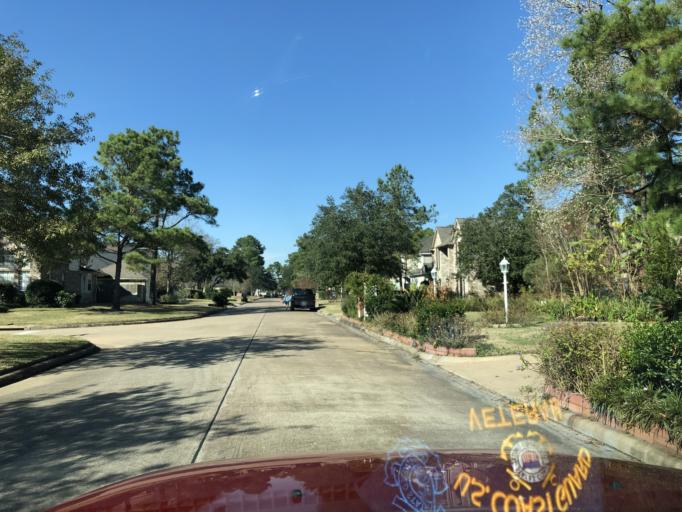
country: US
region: Texas
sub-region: Harris County
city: Tomball
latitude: 30.0311
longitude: -95.5430
